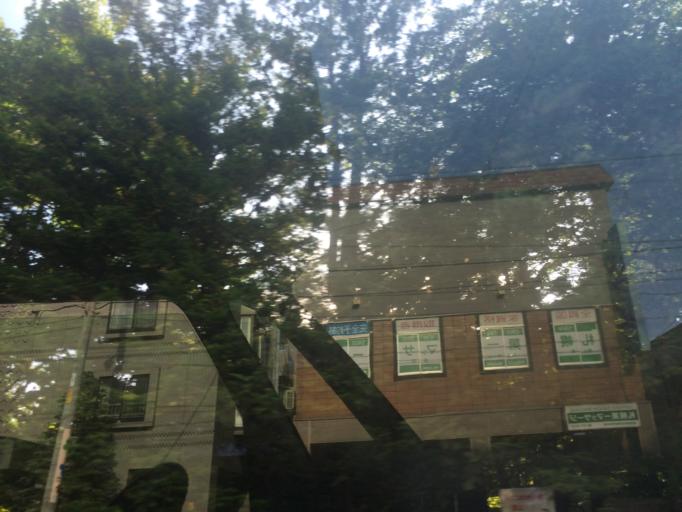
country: JP
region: Hokkaido
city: Sapporo
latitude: 43.0351
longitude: 141.3515
